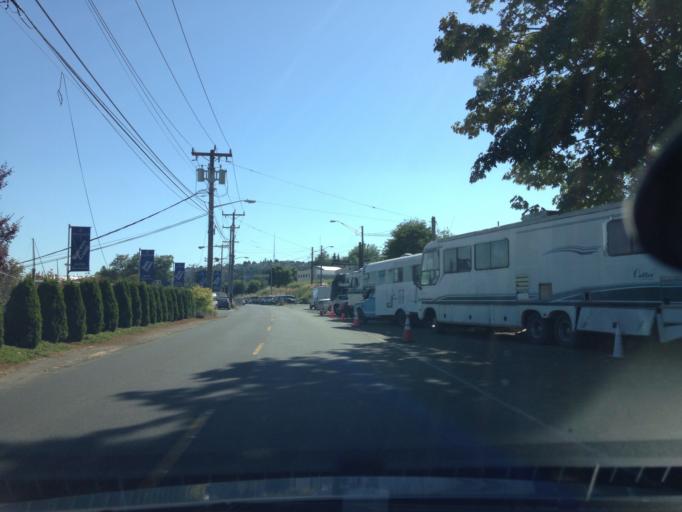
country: US
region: Washington
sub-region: King County
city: Seattle
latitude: 47.6515
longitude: -122.3297
